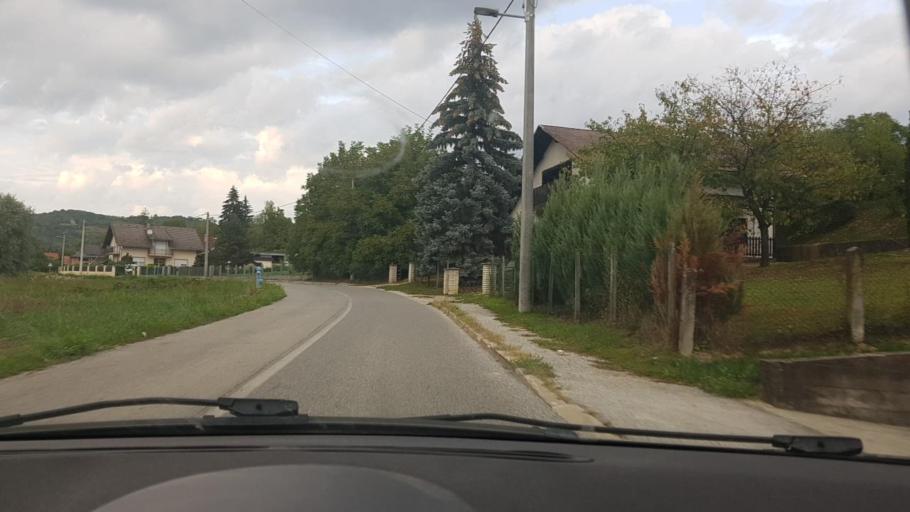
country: HR
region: Krapinsko-Zagorska
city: Marija Bistrica
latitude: 45.9245
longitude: 16.1710
